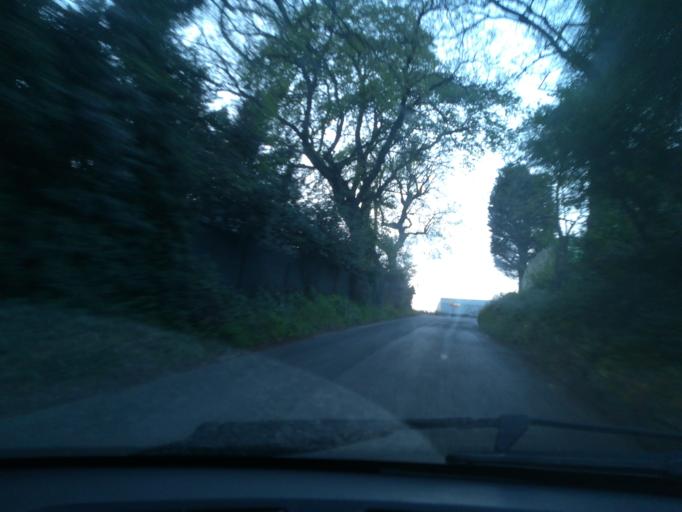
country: IT
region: The Marches
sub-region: Provincia di Macerata
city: Macerata
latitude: 43.2809
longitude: 13.4479
